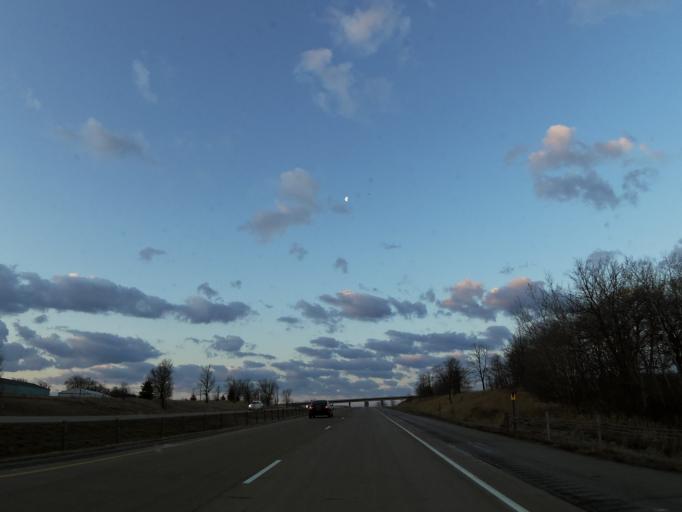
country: US
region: Minnesota
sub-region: Scott County
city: Elko New Market
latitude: 44.5073
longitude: -93.2888
